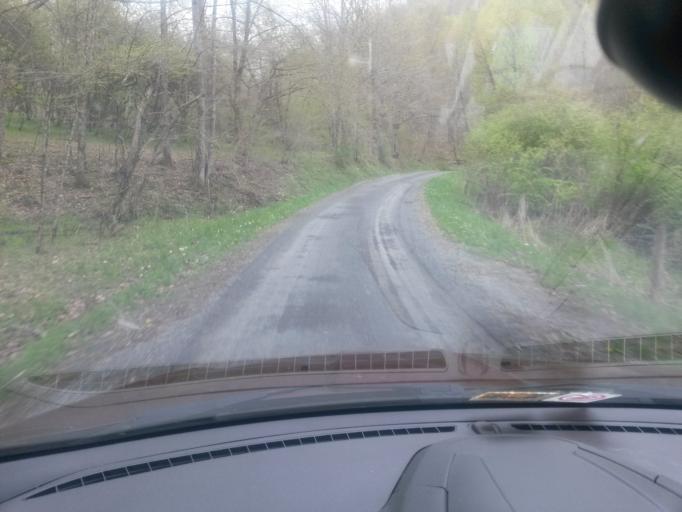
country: US
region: West Virginia
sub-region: Nicholas County
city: Richwood
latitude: 38.0654
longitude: -80.3344
